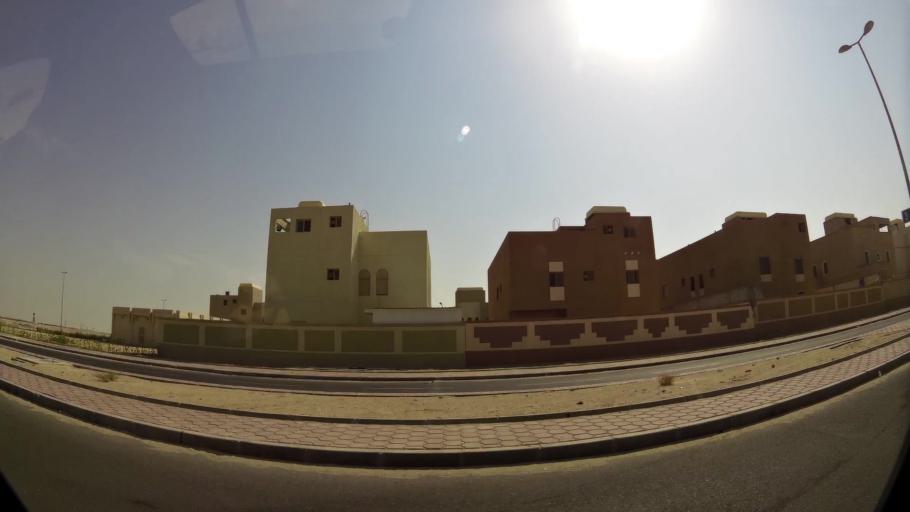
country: KW
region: Al Ahmadi
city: Al Wafrah
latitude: 28.8068
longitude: 48.0639
